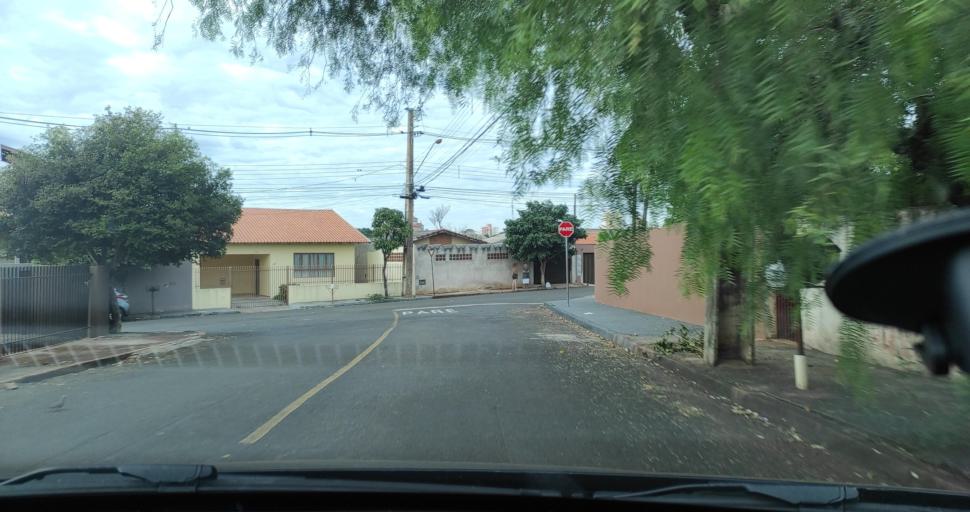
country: BR
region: Parana
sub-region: Ibipora
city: Ibipora
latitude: -23.2592
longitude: -51.0485
